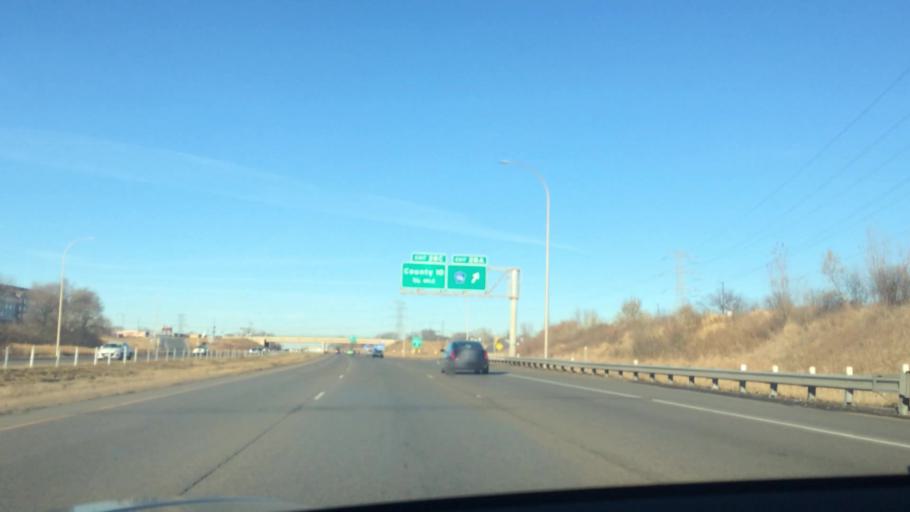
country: US
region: Minnesota
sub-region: Ramsey County
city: New Brighton
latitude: 45.0747
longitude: -93.1852
